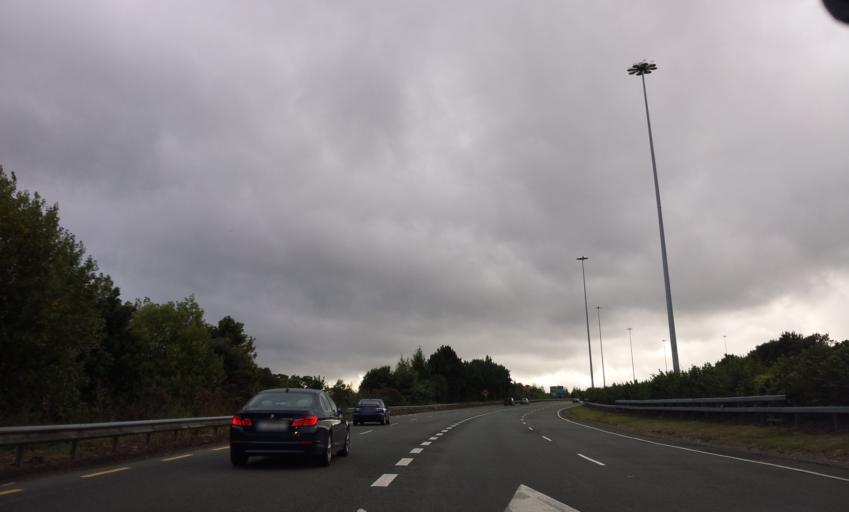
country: IE
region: Munster
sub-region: County Cork
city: Passage West
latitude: 51.9030
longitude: -8.3782
